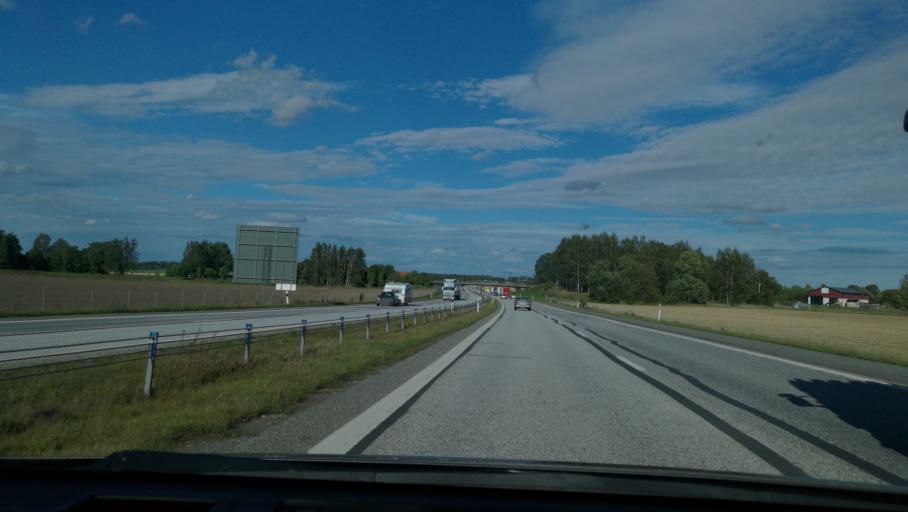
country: SE
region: OErebro
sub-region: Askersunds Kommun
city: Asbro
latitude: 59.0748
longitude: 15.0194
